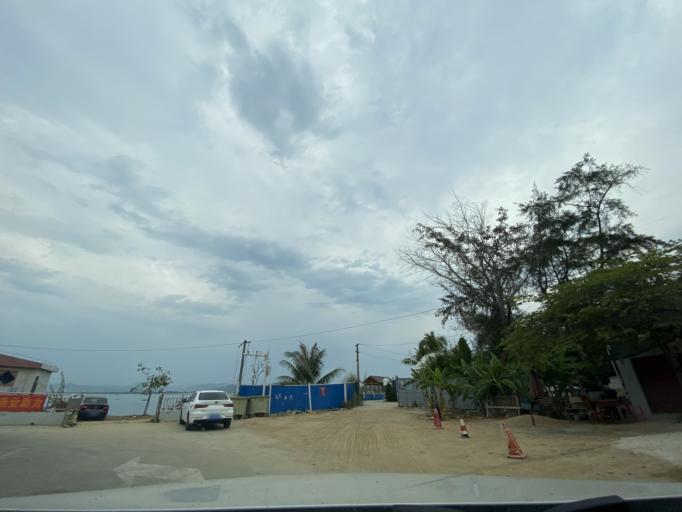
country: CN
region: Hainan
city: Yingzhou
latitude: 18.3857
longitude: 109.8184
